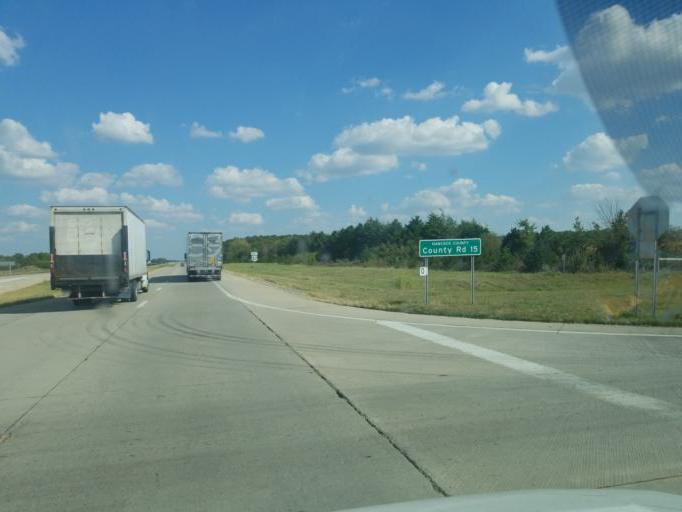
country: US
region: Ohio
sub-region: Allen County
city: Bluffton
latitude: 40.8275
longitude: -83.8802
